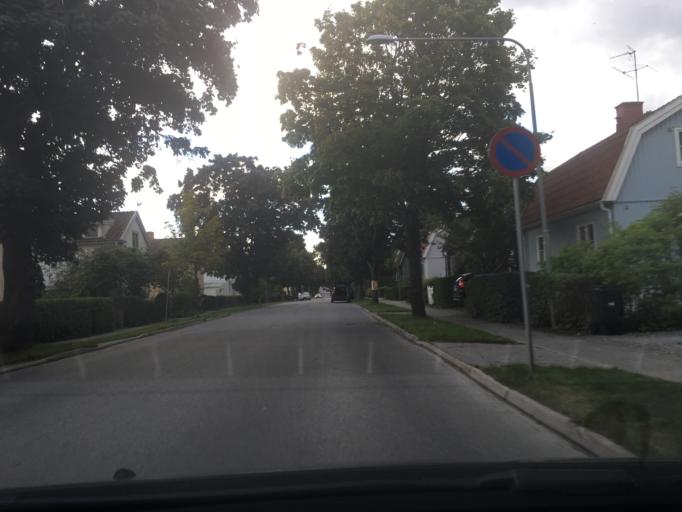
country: SE
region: Stockholm
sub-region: Stockholms Kommun
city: Bromma
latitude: 59.3303
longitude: 17.9370
